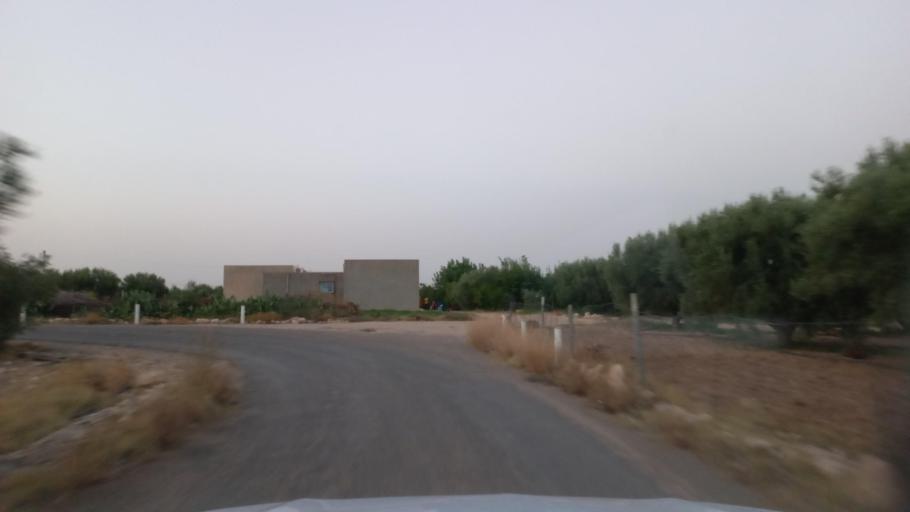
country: TN
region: Al Qasrayn
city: Kasserine
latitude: 35.2725
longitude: 9.0308
